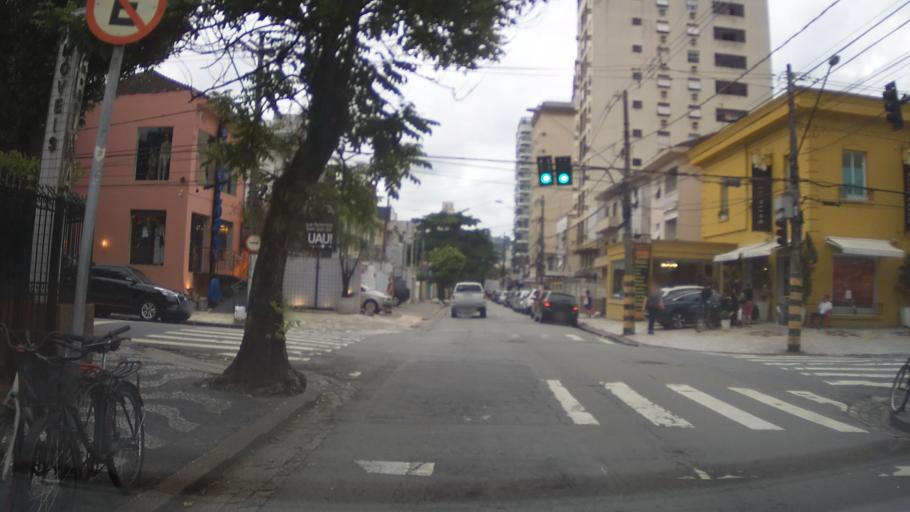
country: BR
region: Sao Paulo
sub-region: Santos
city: Santos
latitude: -23.9610
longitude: -46.3246
